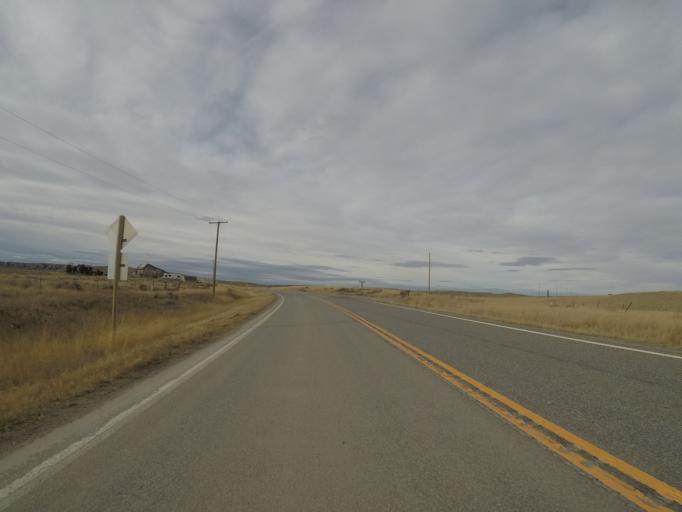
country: US
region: Montana
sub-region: Yellowstone County
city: Laurel
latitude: 45.8415
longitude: -108.7223
